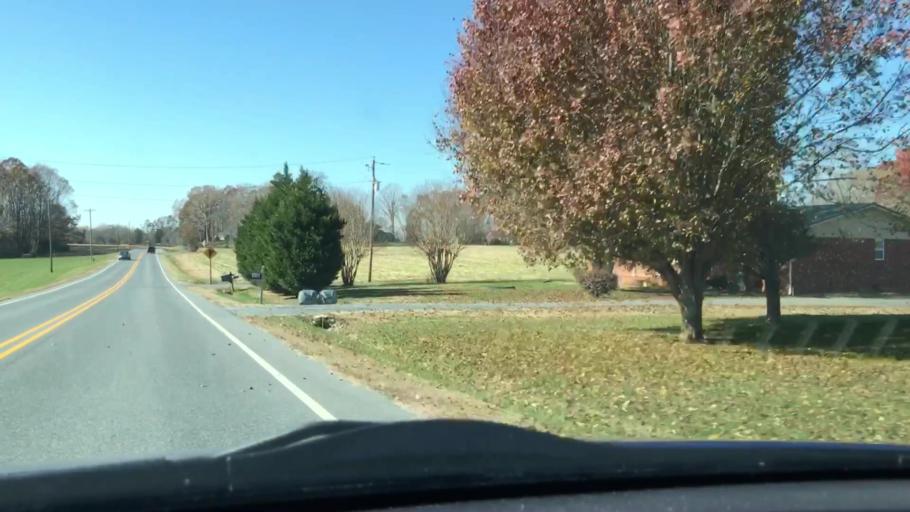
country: US
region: North Carolina
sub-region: Randolph County
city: Asheboro
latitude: 35.6733
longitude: -79.9249
